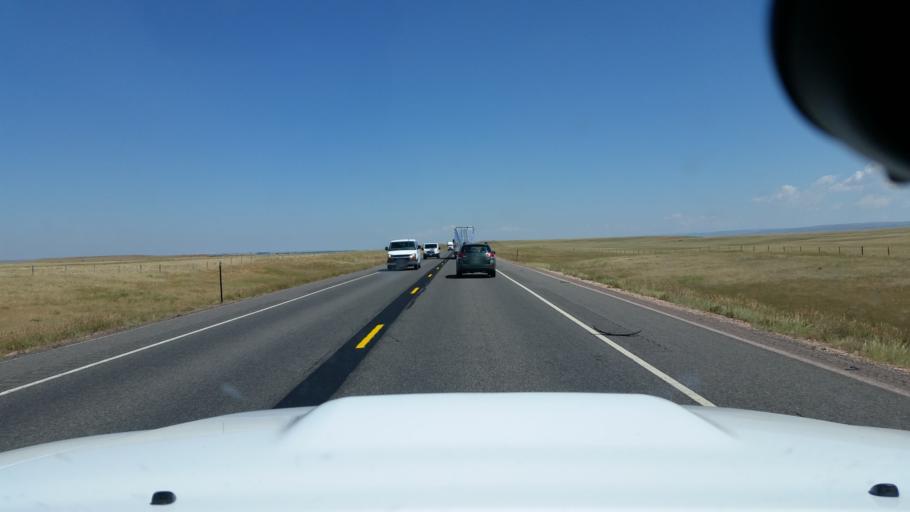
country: US
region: Wyoming
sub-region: Albany County
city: Laramie
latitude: 41.2011
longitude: -105.5989
